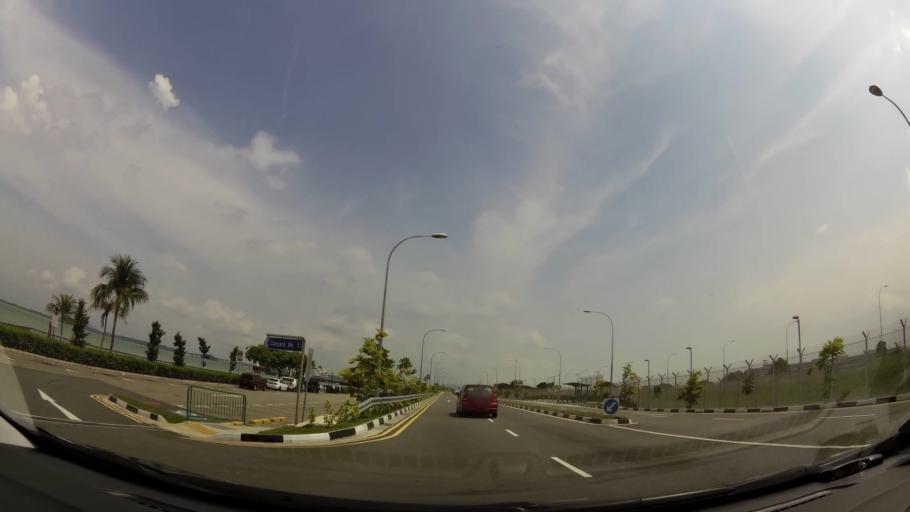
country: MY
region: Johor
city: Kampung Pasir Gudang Baru
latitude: 1.3898
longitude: 103.9956
